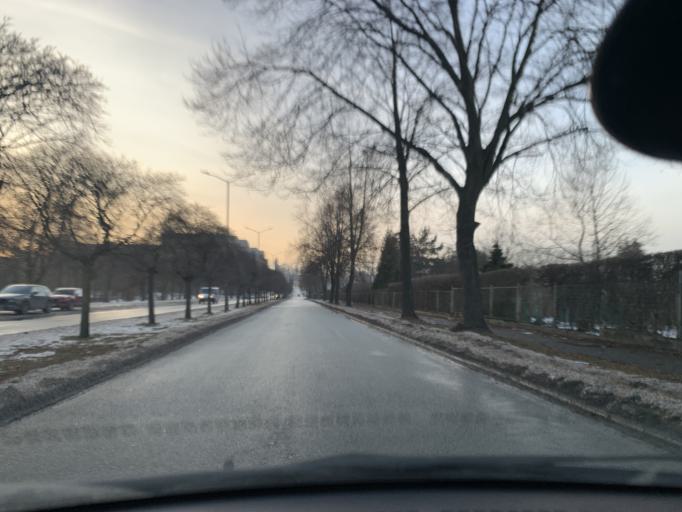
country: PL
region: Silesian Voivodeship
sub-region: Bytom
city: Bytom
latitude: 50.3554
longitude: 18.9059
